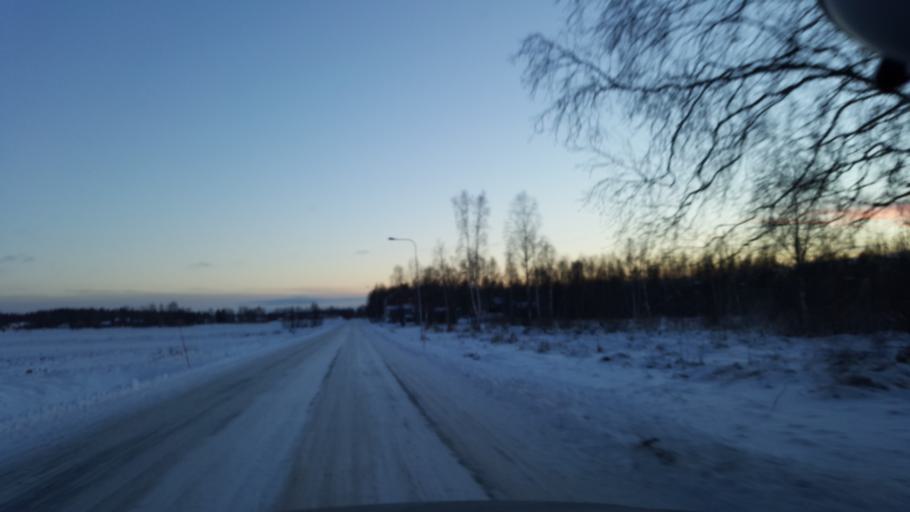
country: SE
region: Norrbotten
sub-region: Lulea Kommun
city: Sodra Sunderbyn
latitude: 65.5397
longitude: 21.9029
